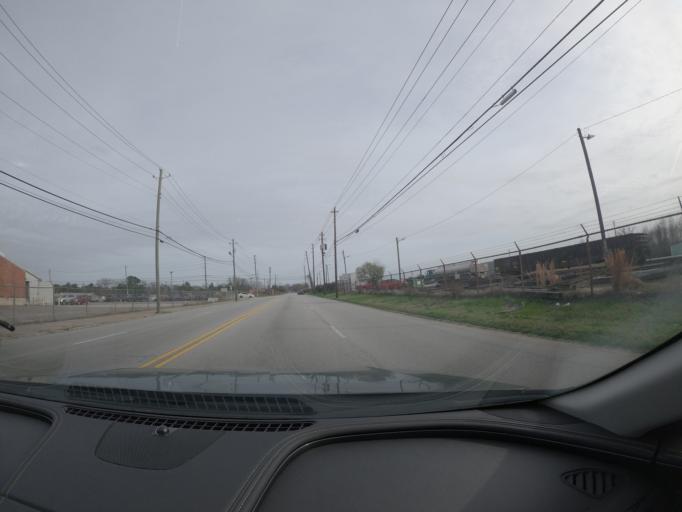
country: US
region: Georgia
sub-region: Richmond County
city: Augusta
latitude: 33.4599
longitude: -81.9633
